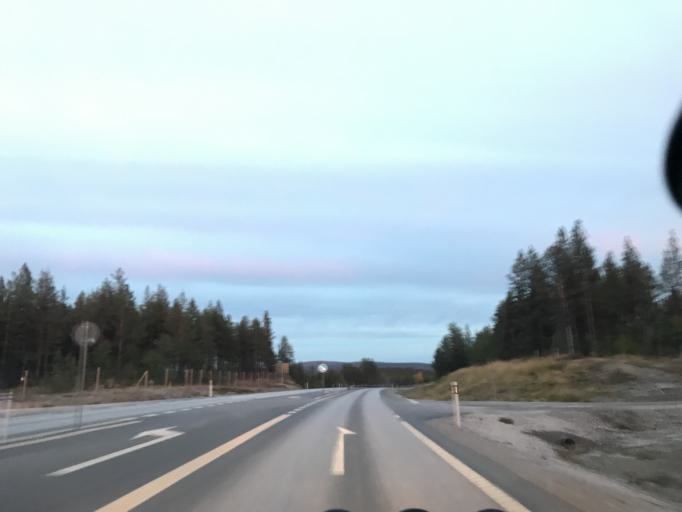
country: SE
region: Norrbotten
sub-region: Gallivare Kommun
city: Malmberget
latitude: 67.6653
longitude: 20.9873
